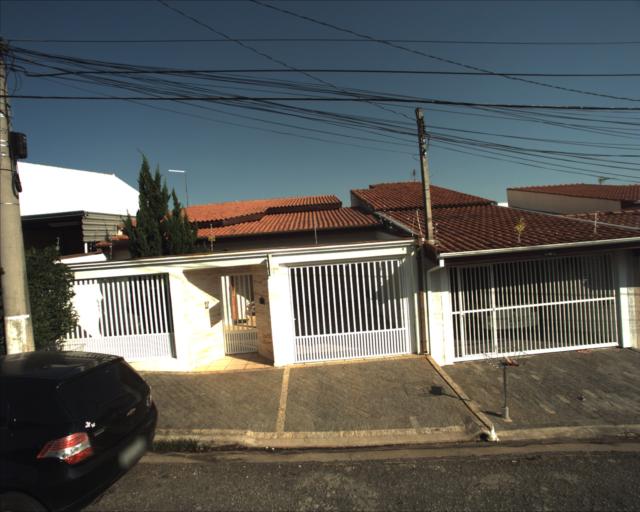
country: BR
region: Sao Paulo
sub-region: Sorocaba
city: Sorocaba
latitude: -23.4959
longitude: -47.4242
